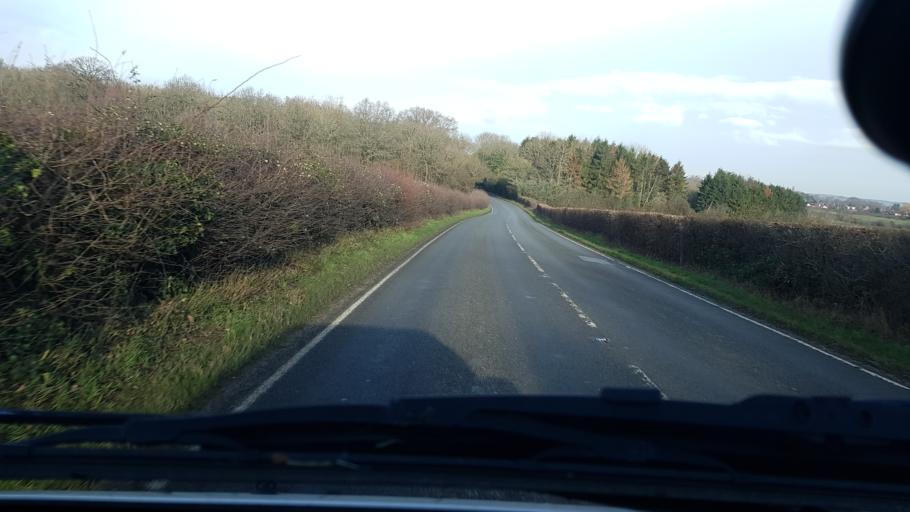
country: GB
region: England
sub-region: Surrey
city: Normandy
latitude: 51.2367
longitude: -0.6715
